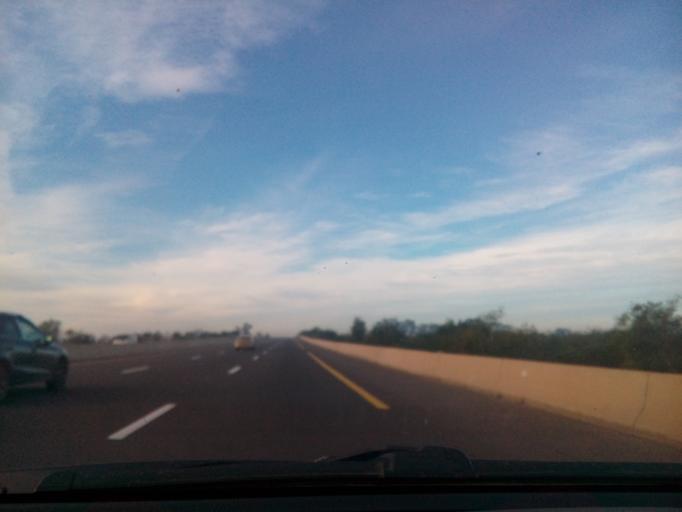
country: DZ
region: Mascara
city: Mascara
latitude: 35.6199
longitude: 0.0414
